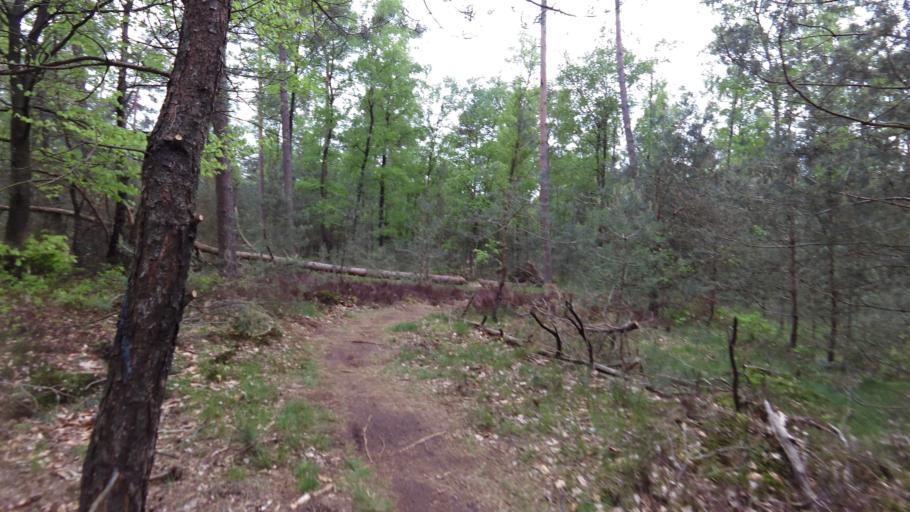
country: NL
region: Gelderland
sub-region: Gemeente Brummen
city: Eerbeek
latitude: 52.0735
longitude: 6.0470
